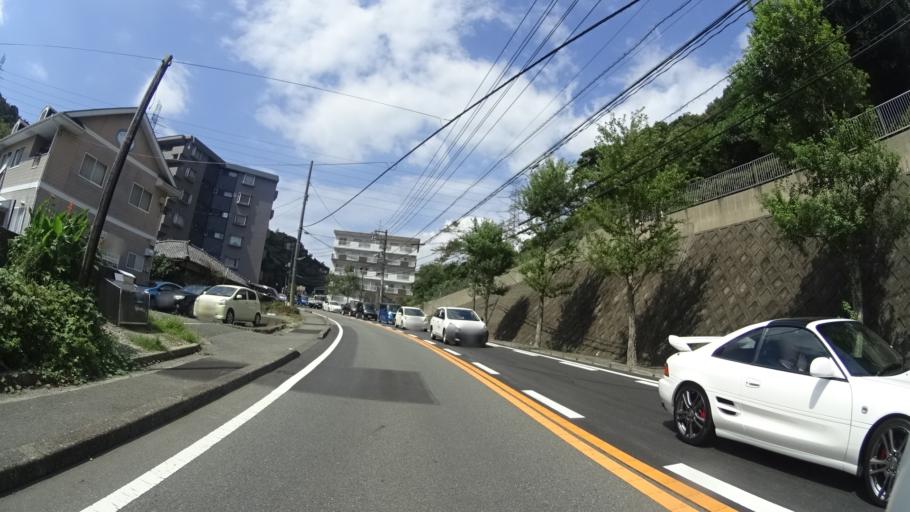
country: JP
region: Yamaguchi
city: Shimonoseki
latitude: 33.9687
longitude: 130.9544
